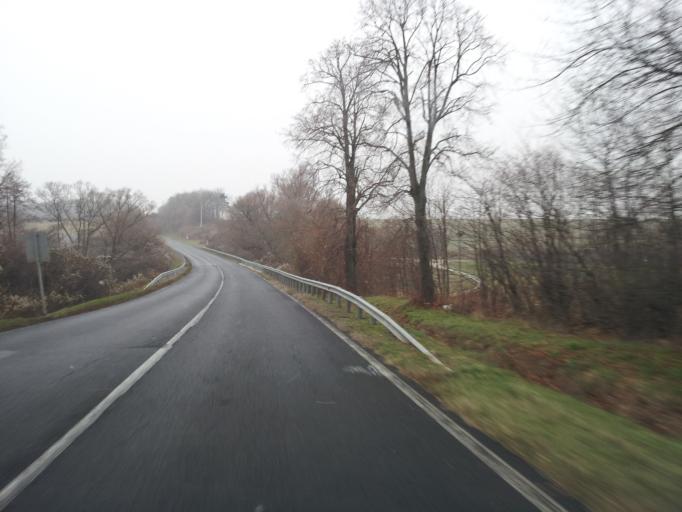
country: HU
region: Veszprem
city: Urkut
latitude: 47.1518
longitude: 17.6269
